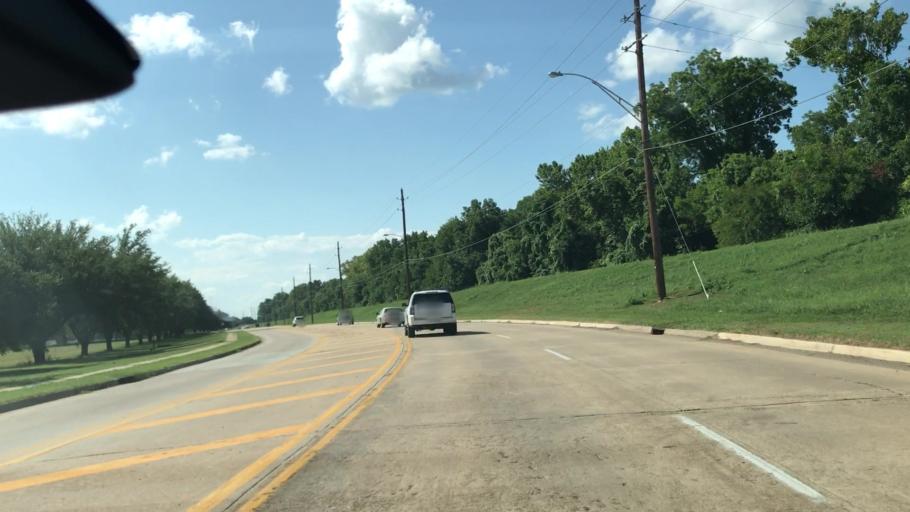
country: US
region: Louisiana
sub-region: Bossier Parish
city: Bossier City
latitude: 32.4270
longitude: -93.6951
